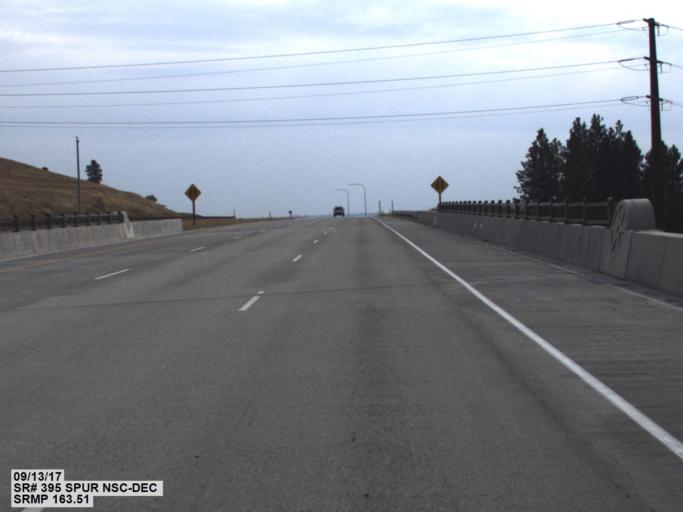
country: US
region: Washington
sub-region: Spokane County
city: Mead
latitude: 47.7431
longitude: -117.3606
